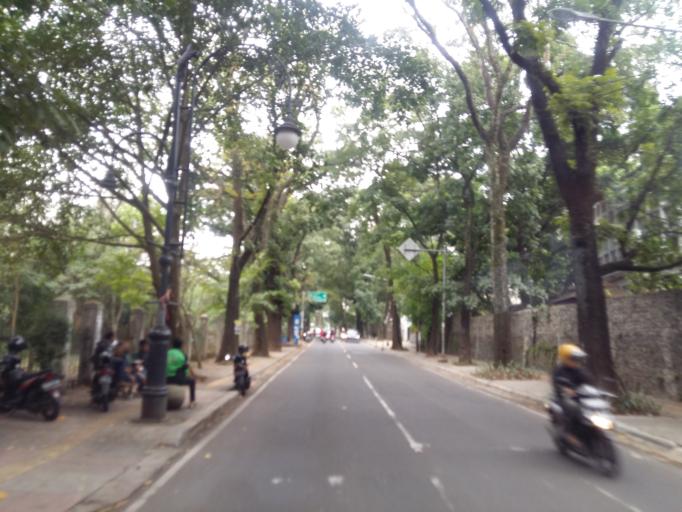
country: ID
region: West Java
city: Bandung
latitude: -6.8877
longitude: 107.6088
